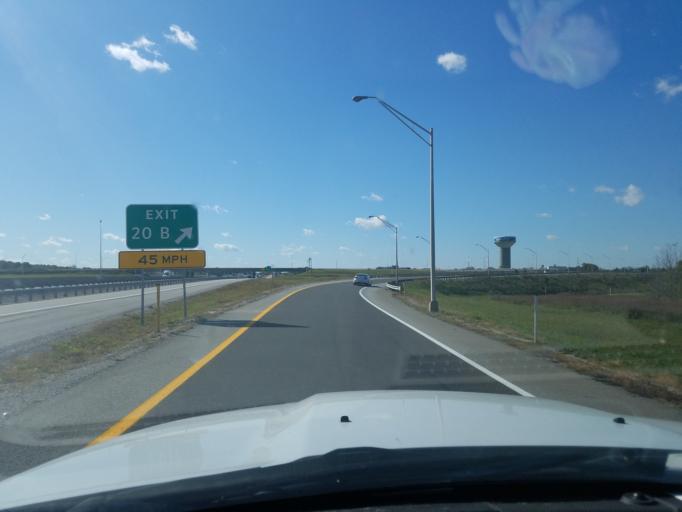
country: US
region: Kentucky
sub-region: Warren County
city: Plano
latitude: 36.9137
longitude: -86.4307
